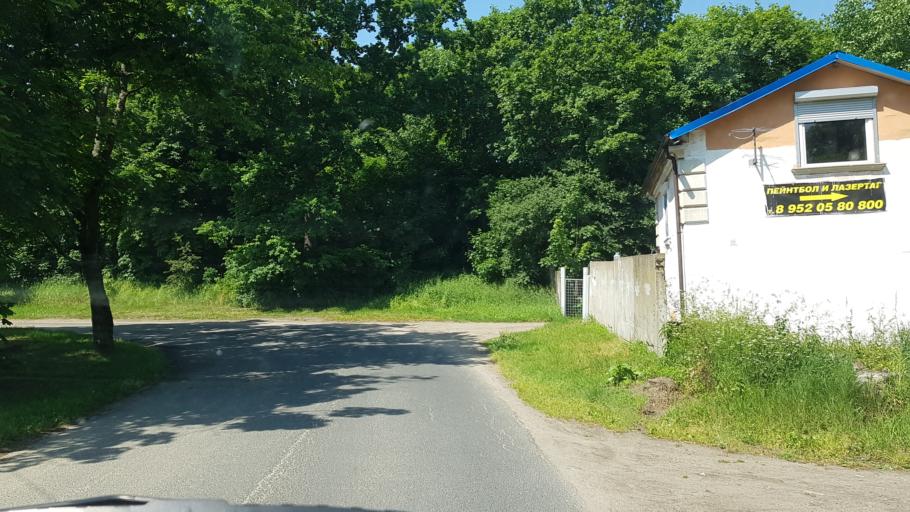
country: RU
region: Kaliningrad
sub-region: Gorod Kaliningrad
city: Baltiysk
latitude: 54.6462
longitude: 19.8842
